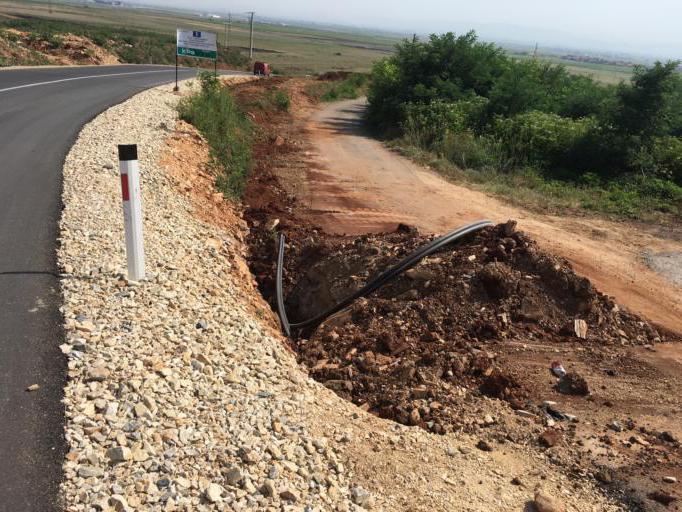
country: XK
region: Pristina
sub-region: Komuna e Gracanices
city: Glanica
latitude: 42.5424
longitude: 21.0143
